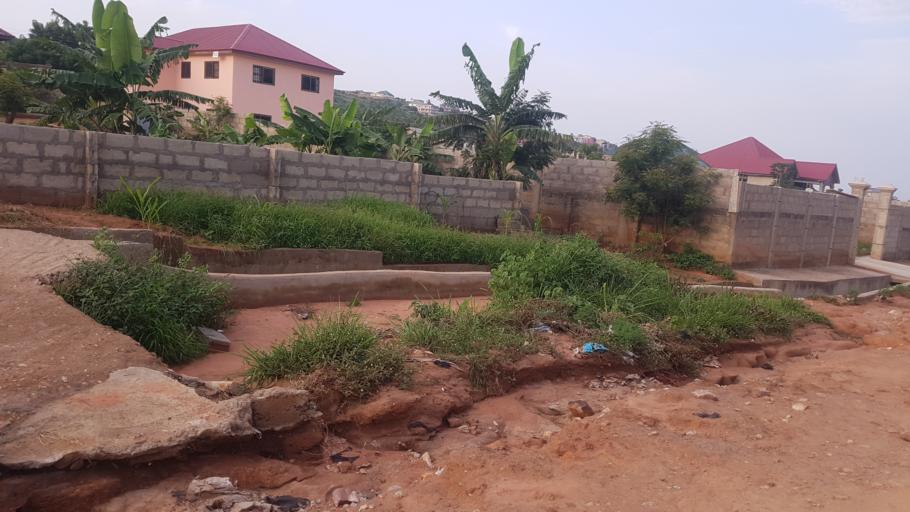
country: GH
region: Greater Accra
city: Gbawe
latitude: 5.5227
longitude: -0.3419
